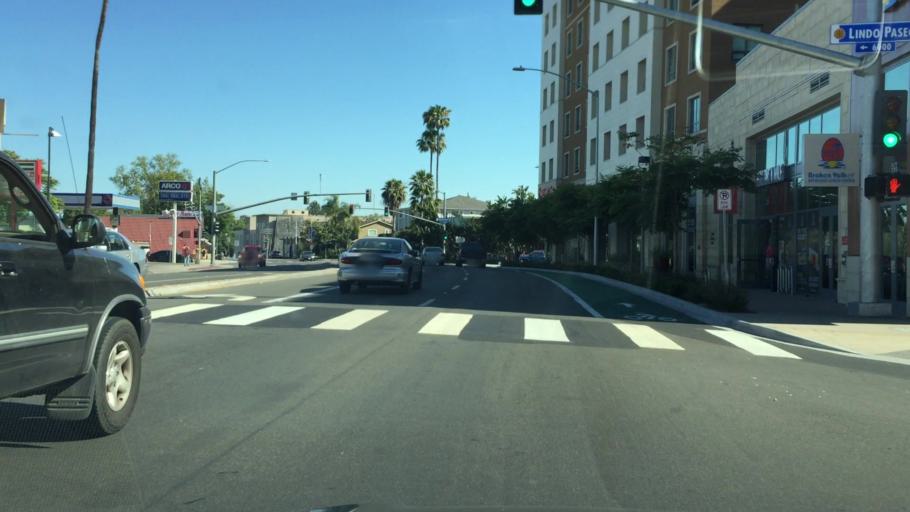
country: US
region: California
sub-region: San Diego County
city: La Mesa
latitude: 32.7716
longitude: -117.0701
